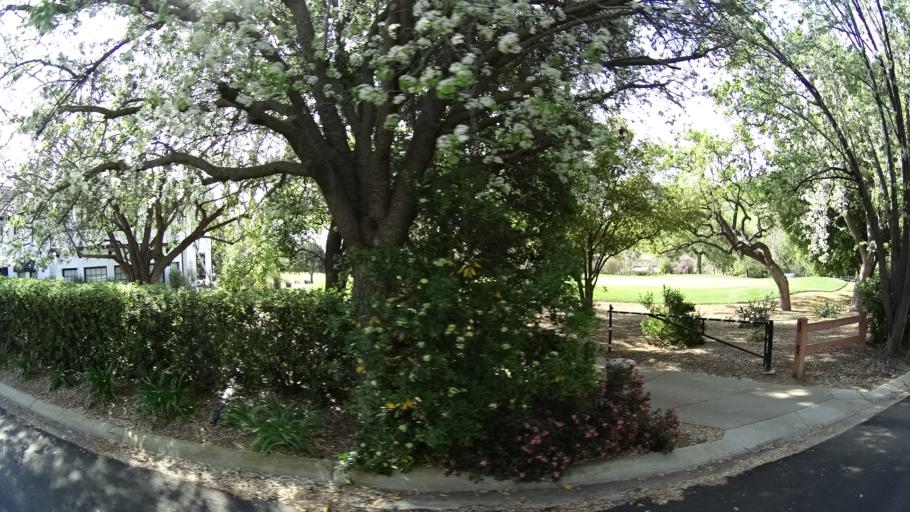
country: US
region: California
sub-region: Ventura County
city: Oak Park
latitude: 34.1894
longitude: -118.7950
